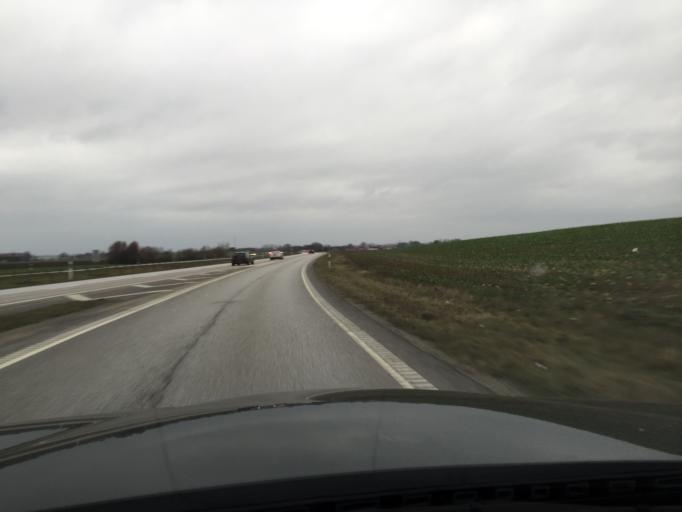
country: SE
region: Skane
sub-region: Malmo
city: Oxie
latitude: 55.5913
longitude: 13.1169
